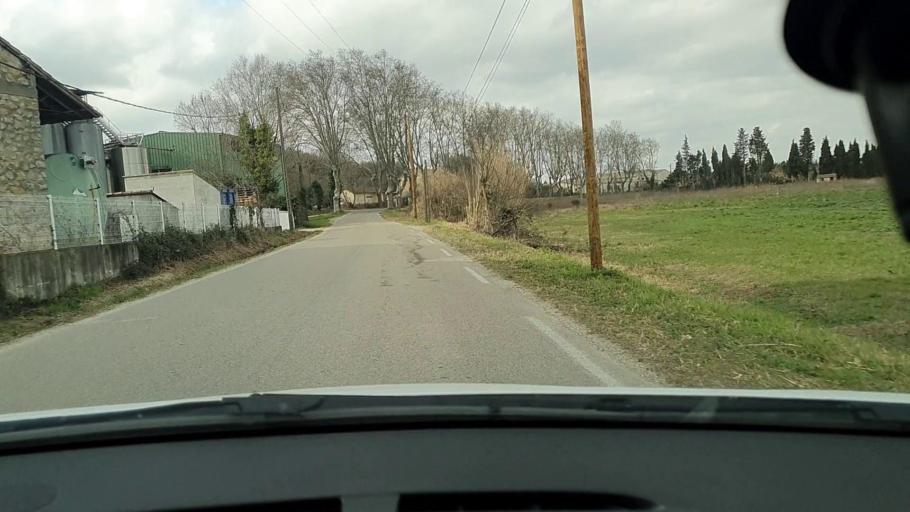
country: FR
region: Languedoc-Roussillon
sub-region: Departement du Gard
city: Meynes
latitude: 43.8712
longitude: 4.5781
